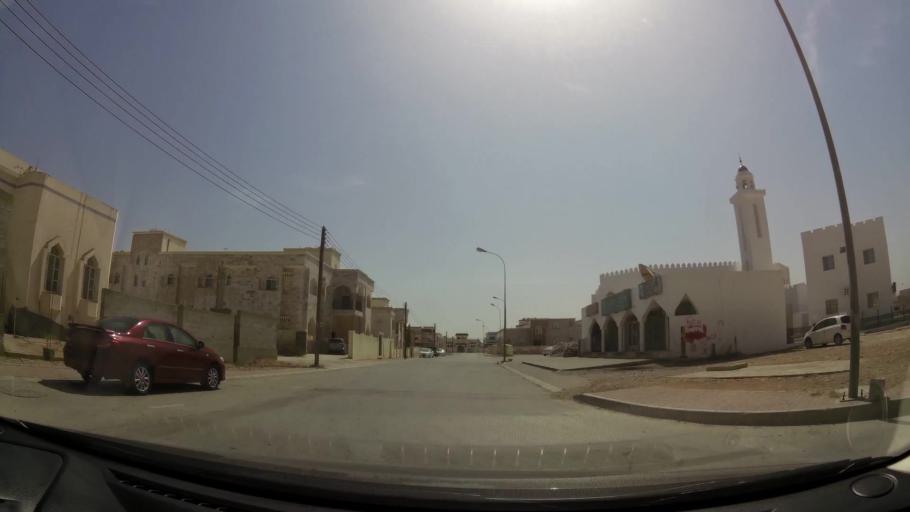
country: OM
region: Zufar
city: Salalah
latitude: 17.0433
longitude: 54.1591
